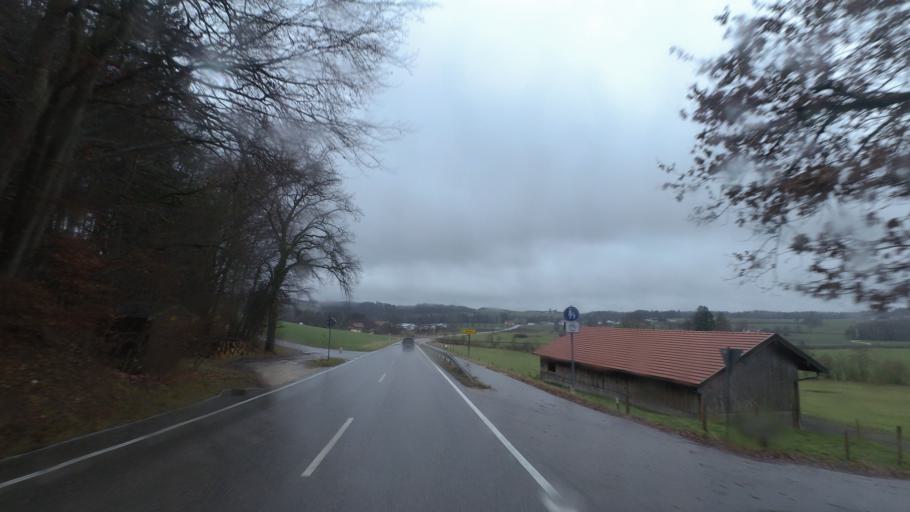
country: DE
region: Bavaria
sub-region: Upper Bavaria
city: Sankt Leonhard am Wonneberg
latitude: 47.9324
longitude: 12.7013
